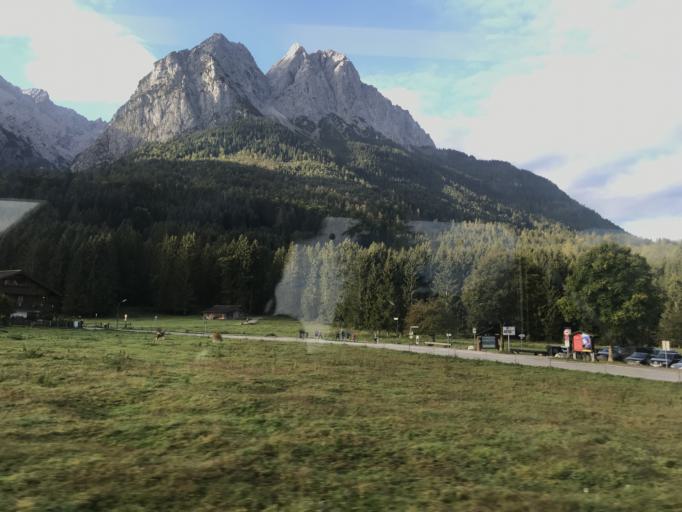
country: DE
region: Bavaria
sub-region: Upper Bavaria
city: Grainau
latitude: 47.4687
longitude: 11.0415
